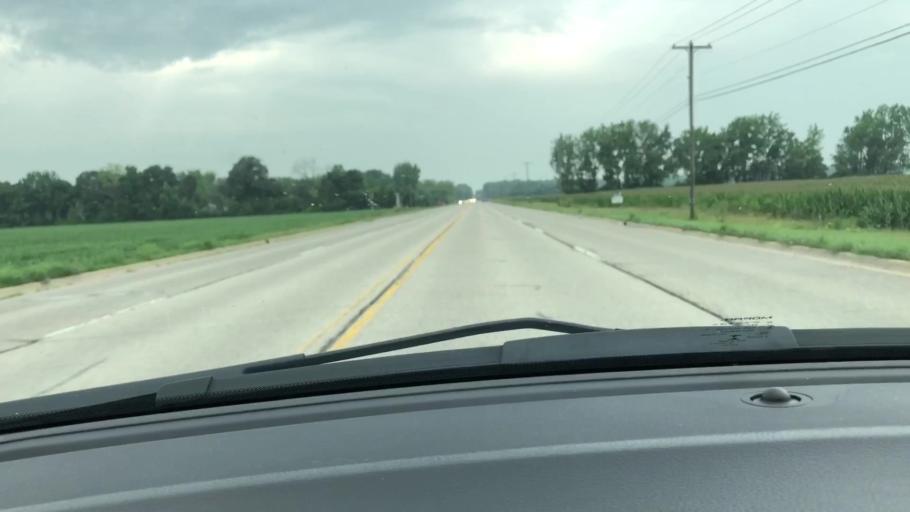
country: US
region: Michigan
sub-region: Saginaw County
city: Freeland
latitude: 43.4812
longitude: -84.0782
